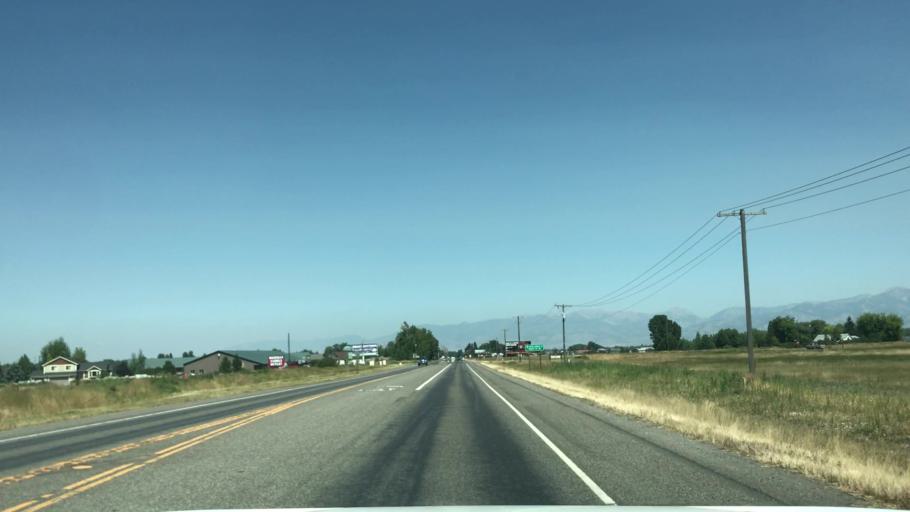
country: US
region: Montana
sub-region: Gallatin County
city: Four Corners
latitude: 45.6437
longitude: -111.1953
